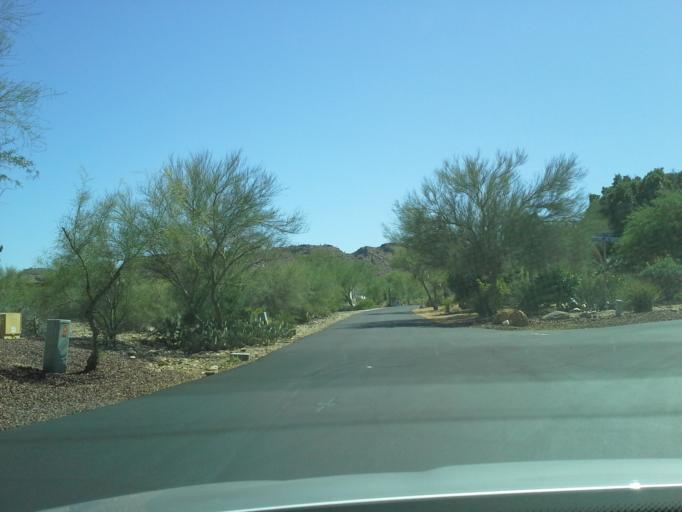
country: US
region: Arizona
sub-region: Maricopa County
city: Paradise Valley
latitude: 33.5527
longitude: -111.9477
